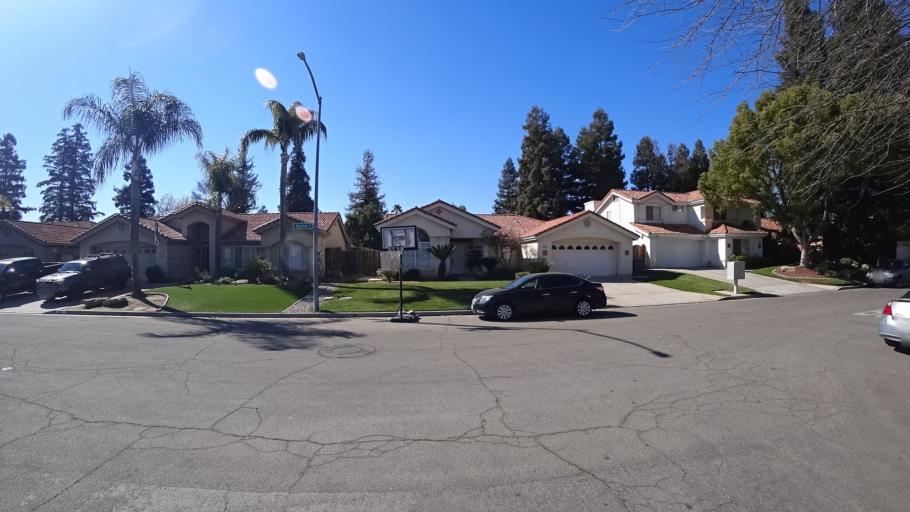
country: US
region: California
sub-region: Fresno County
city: Clovis
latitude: 36.8642
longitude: -119.7519
